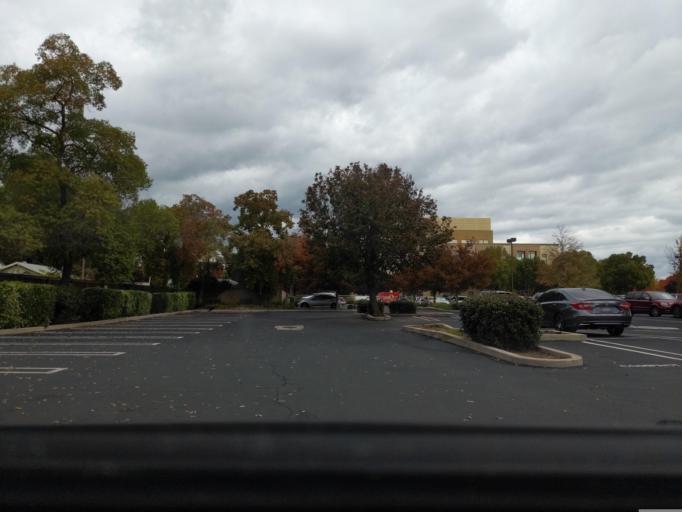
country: US
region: California
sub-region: Stanislaus County
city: Modesto
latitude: 37.6517
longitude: -120.9743
